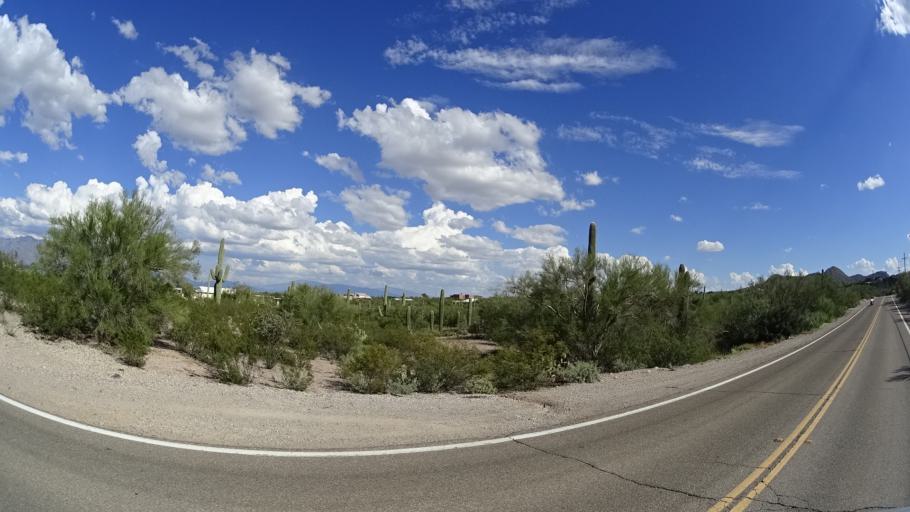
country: US
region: Arizona
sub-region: Pima County
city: Flowing Wells
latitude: 32.2619
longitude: -111.0628
